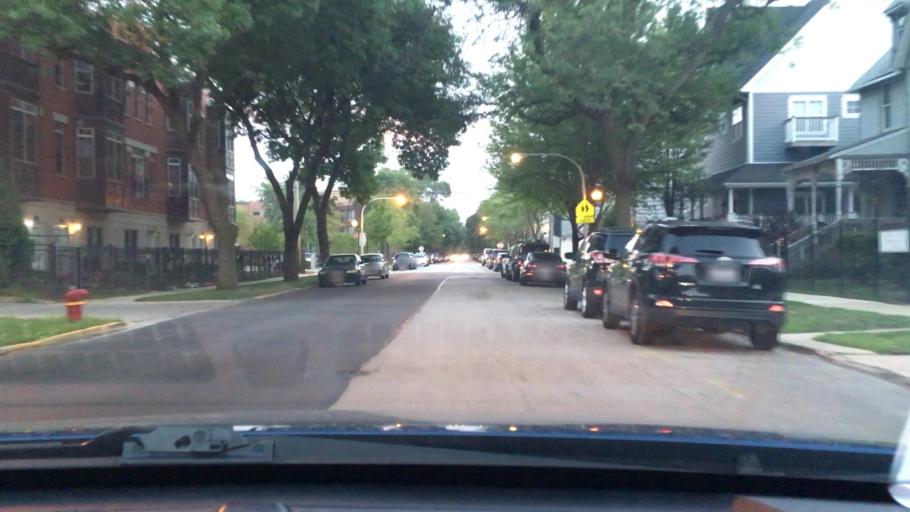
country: US
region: Illinois
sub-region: Cook County
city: Chicago
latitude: 41.8108
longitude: -87.5993
